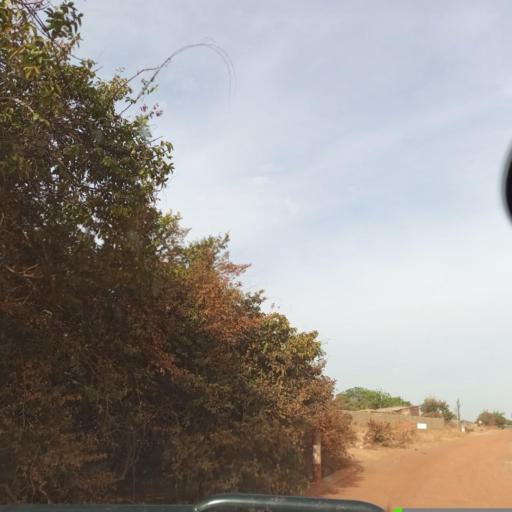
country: ML
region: Koulikoro
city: Koulikoro
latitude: 13.1086
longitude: -7.6490
